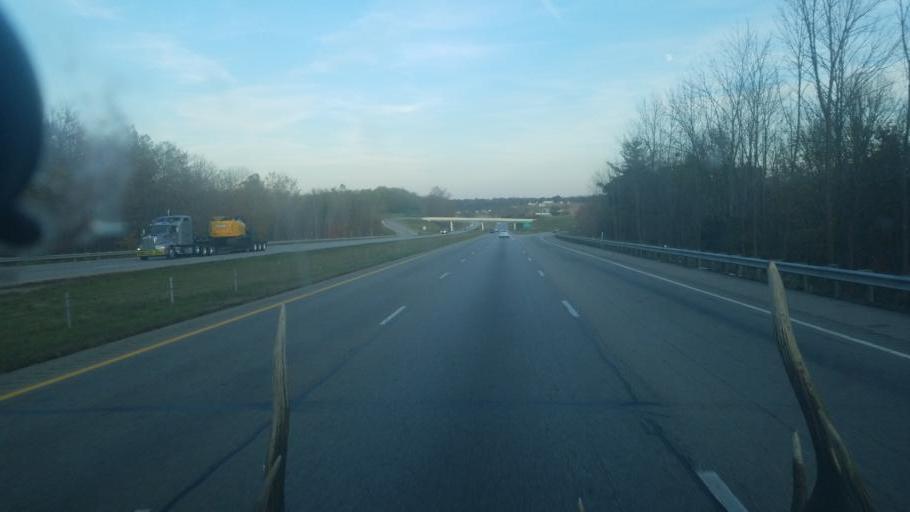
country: US
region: Ohio
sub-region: Perry County
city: Somerset
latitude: 39.9361
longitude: -82.2614
